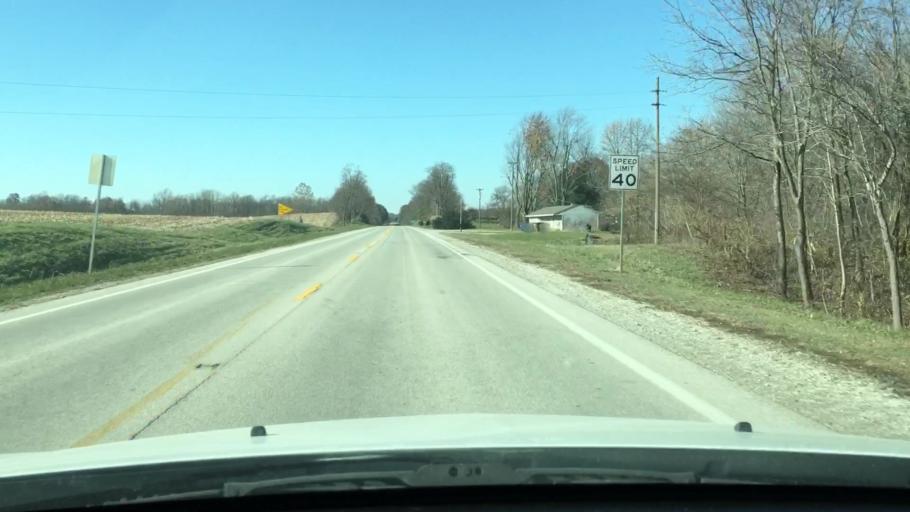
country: US
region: Illinois
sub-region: Pike County
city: Griggsville
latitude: 39.6201
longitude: -90.6830
